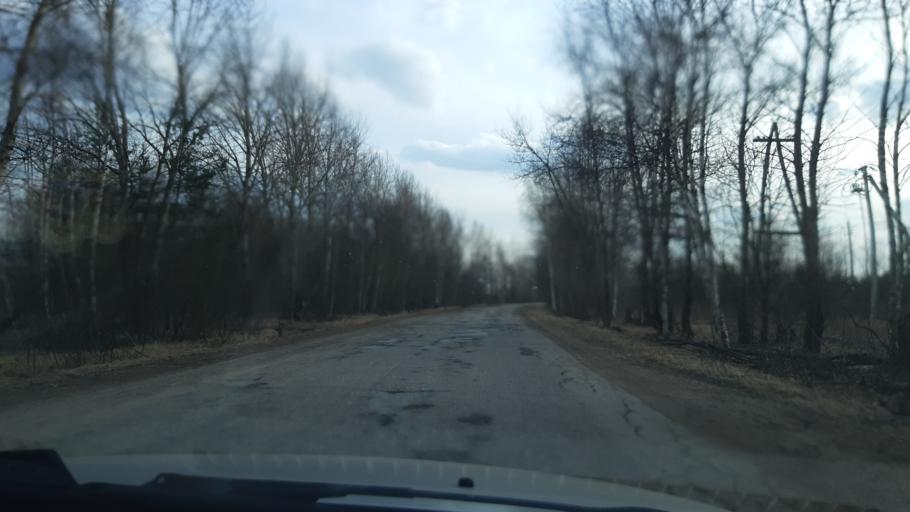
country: RU
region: Vladimir
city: Nikologory
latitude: 56.1083
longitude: 41.9822
